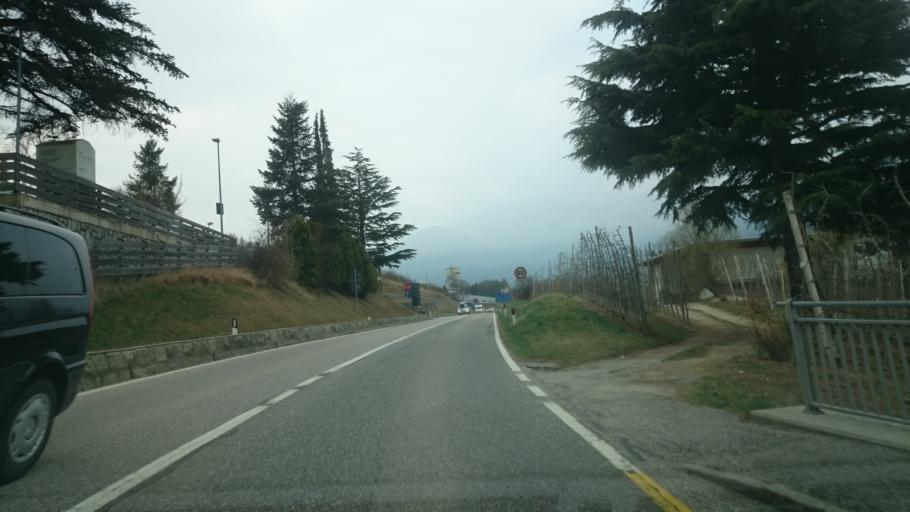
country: IT
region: Trentino-Alto Adige
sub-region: Bolzano
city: Naz-Sciaves - Natz-Schabs
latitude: 46.7691
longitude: 11.6643
